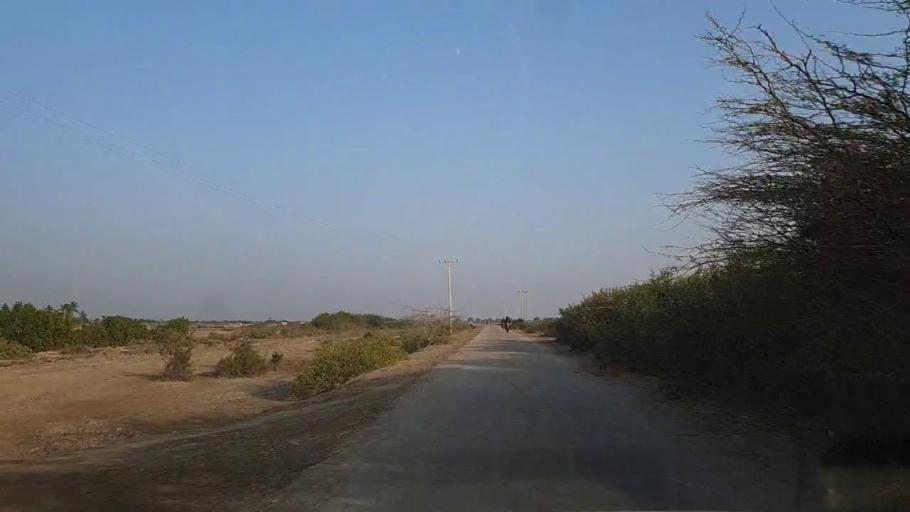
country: PK
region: Sindh
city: Keti Bandar
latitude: 24.2799
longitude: 67.6290
